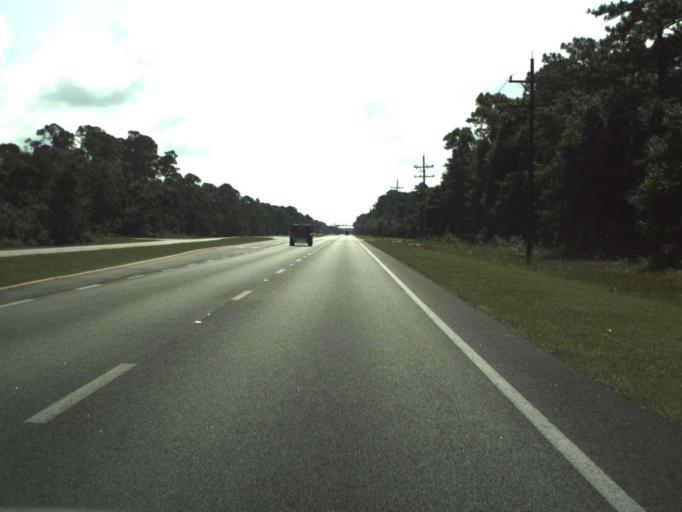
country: US
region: Florida
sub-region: Volusia County
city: Glencoe
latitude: 29.0129
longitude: -80.9770
